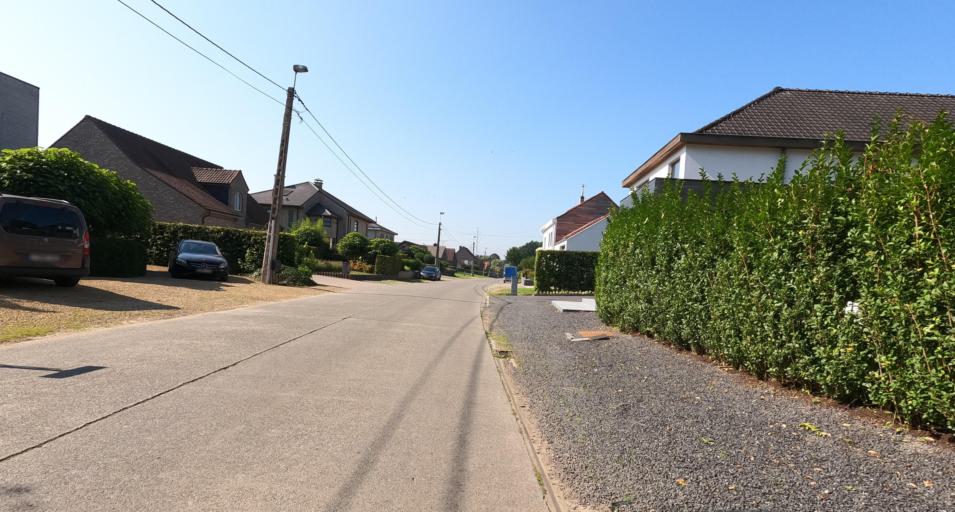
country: BE
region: Flanders
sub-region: Provincie Oost-Vlaanderen
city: Temse
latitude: 51.1432
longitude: 4.2230
